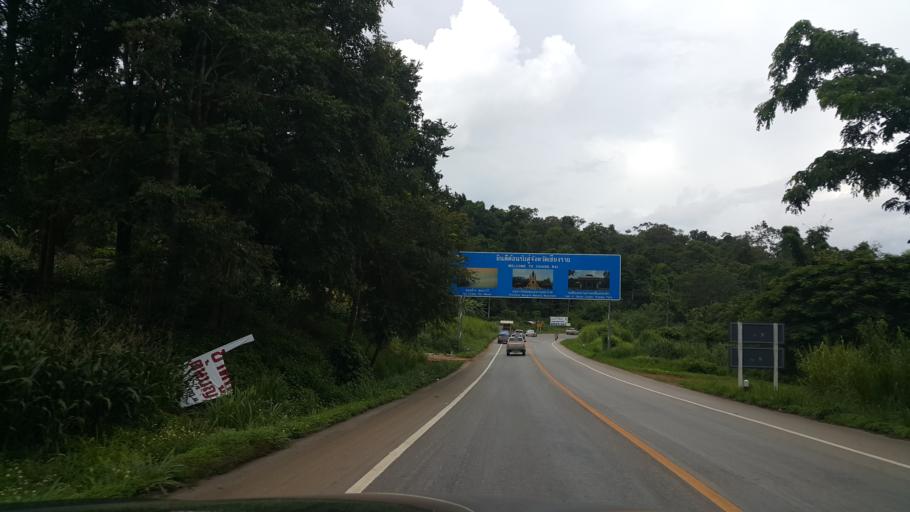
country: TH
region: Lampang
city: Wang Nuea
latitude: 19.1070
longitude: 99.4516
